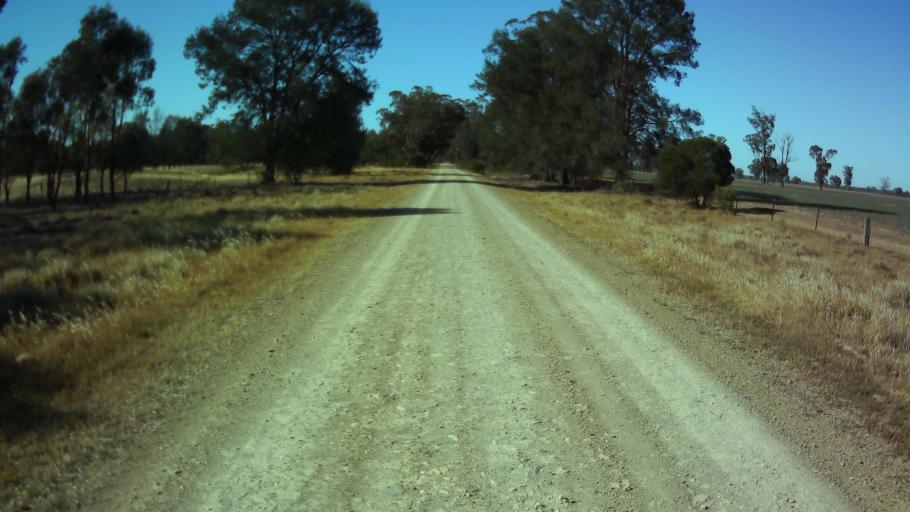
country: AU
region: New South Wales
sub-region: Weddin
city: Grenfell
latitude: -33.9342
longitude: 147.8723
